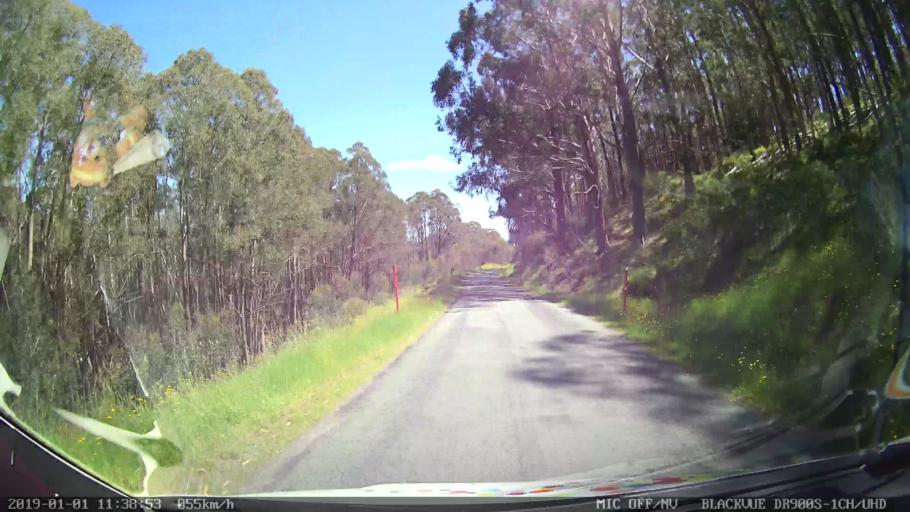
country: AU
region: New South Wales
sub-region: Snowy River
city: Jindabyne
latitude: -35.9311
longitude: 148.3865
